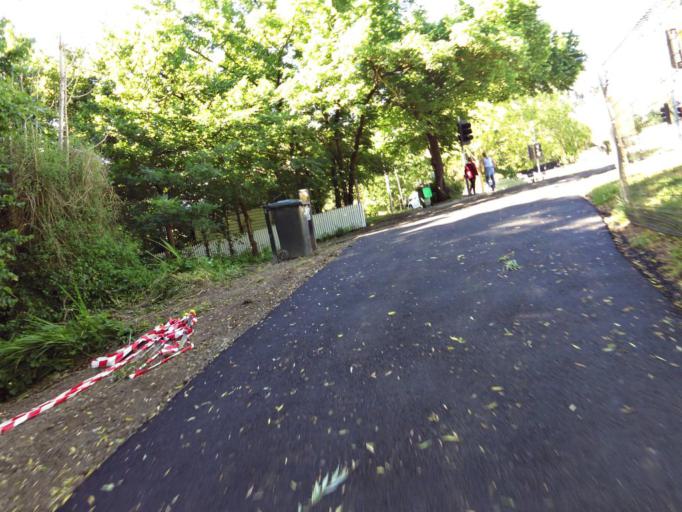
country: AU
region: Victoria
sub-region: Nillumbik
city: Eltham
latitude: -37.7246
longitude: 145.1459
